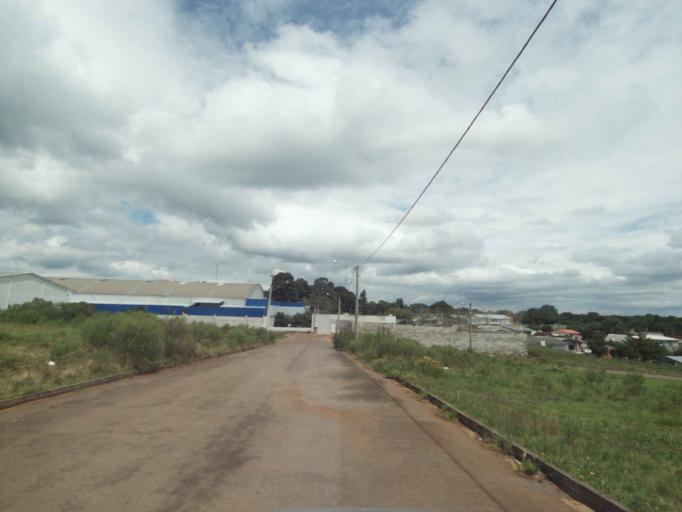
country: BR
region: Rio Grande do Sul
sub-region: Lagoa Vermelha
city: Lagoa Vermelha
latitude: -28.2198
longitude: -51.5161
